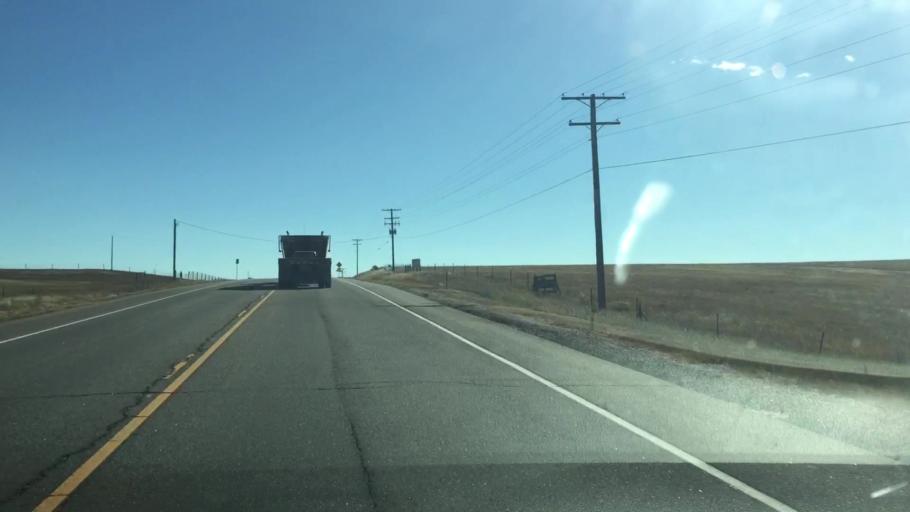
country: US
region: Colorado
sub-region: Elbert County
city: Ponderosa Park
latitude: 39.3620
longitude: -104.6613
